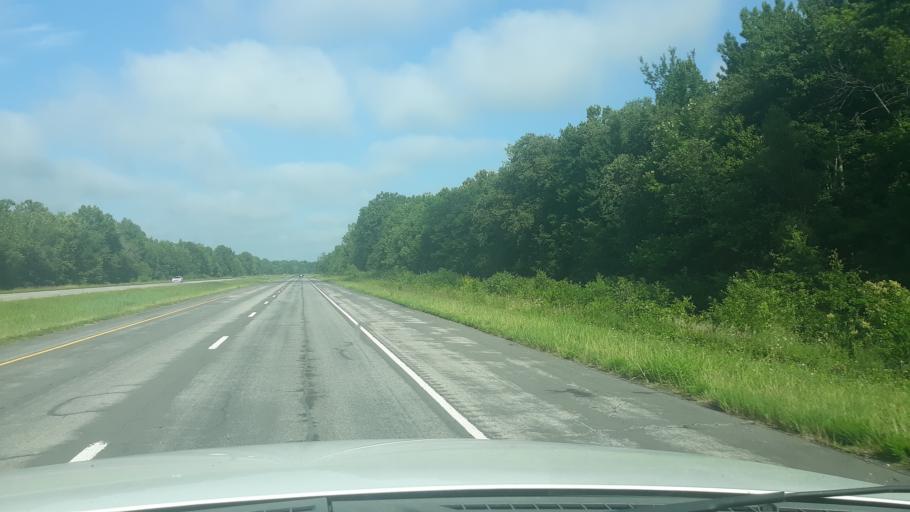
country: US
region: Illinois
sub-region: Saline County
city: Carrier Mills
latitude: 37.7343
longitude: -88.6842
